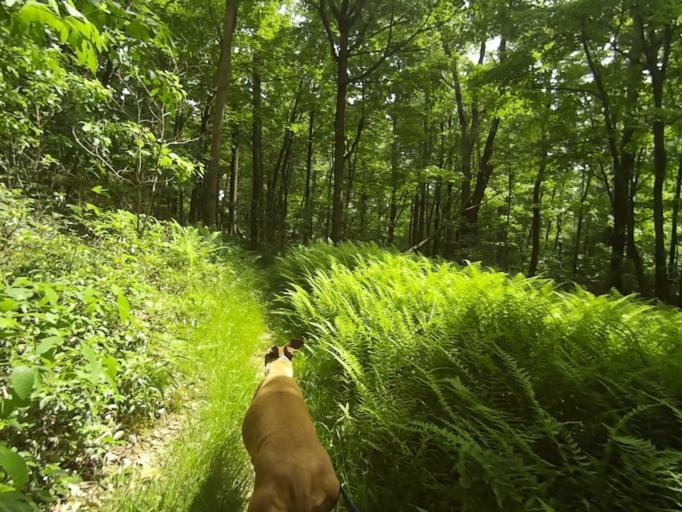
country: US
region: Pennsylvania
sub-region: Centre County
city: Stormstown
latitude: 40.9178
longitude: -78.0537
